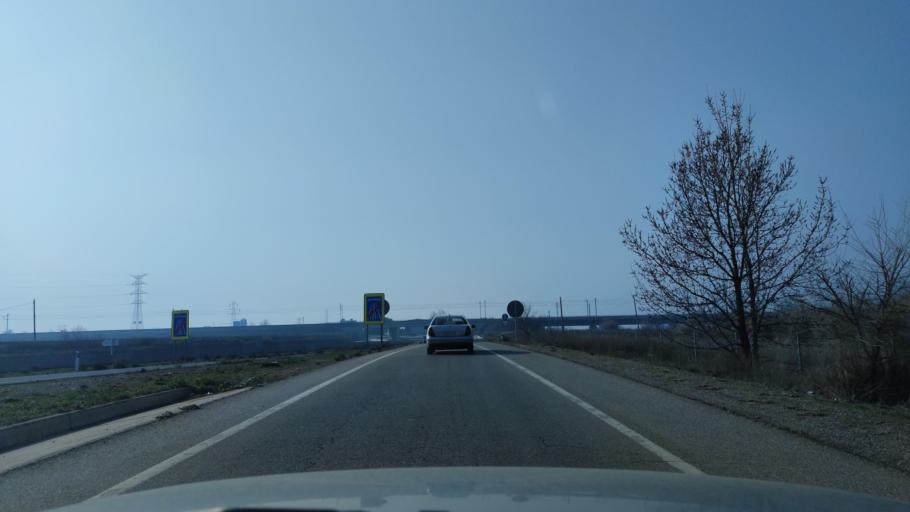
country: ES
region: Catalonia
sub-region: Provincia de Lleida
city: Lleida
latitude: 41.5868
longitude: 0.6288
